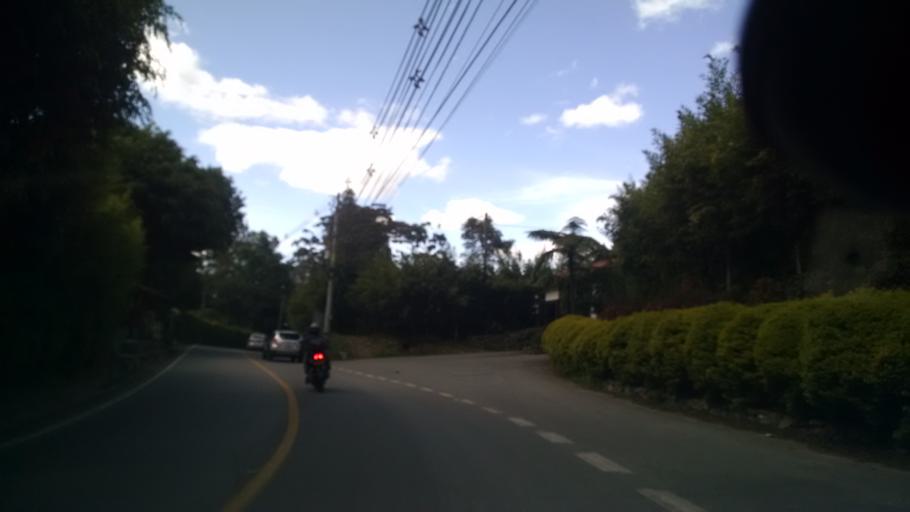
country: CO
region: Antioquia
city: El Retiro
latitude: 6.0782
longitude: -75.4955
